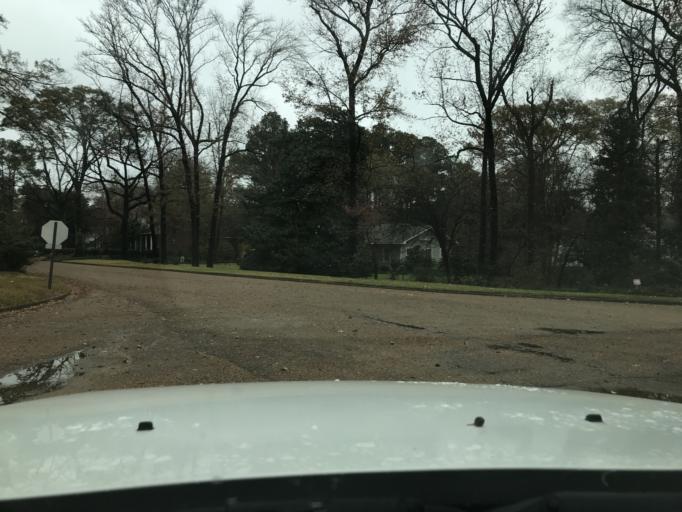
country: US
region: Mississippi
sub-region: Rankin County
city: Flowood
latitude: 32.3418
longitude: -90.1694
